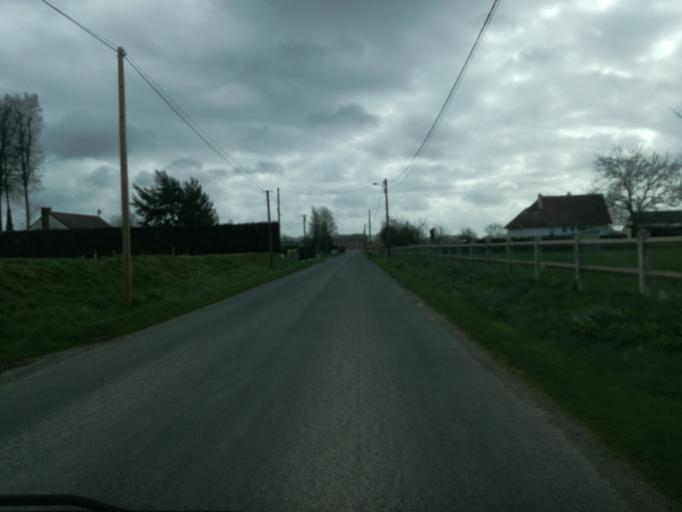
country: FR
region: Haute-Normandie
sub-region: Departement de la Seine-Maritime
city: Yebleron
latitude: 49.6624
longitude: 0.5091
